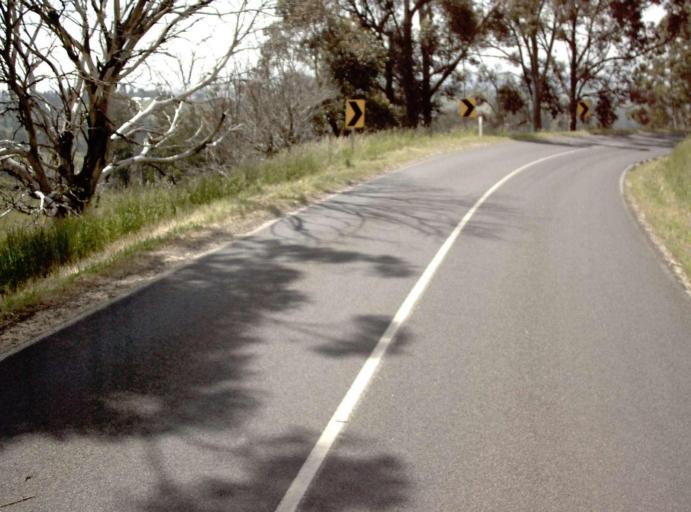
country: AU
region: Victoria
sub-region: Latrobe
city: Traralgon
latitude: -38.3521
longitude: 146.5680
